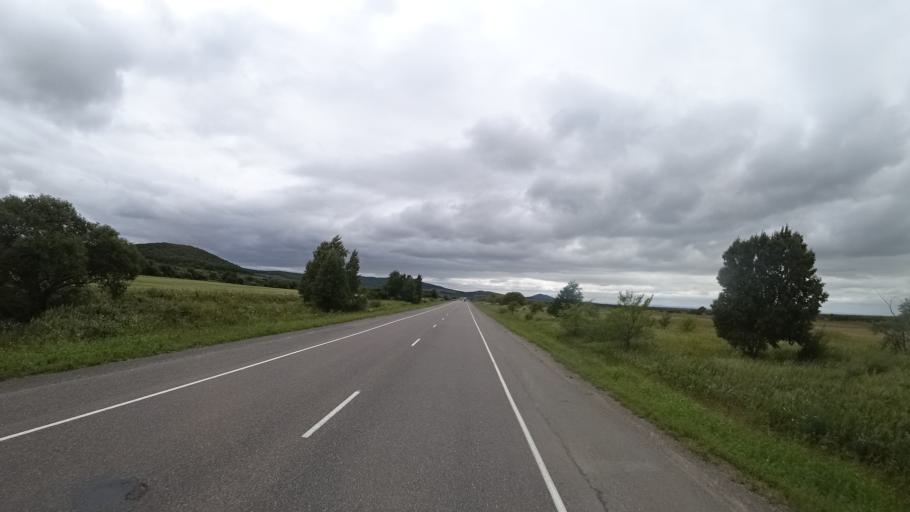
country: RU
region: Primorskiy
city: Chernigovka
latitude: 44.2970
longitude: 132.5208
